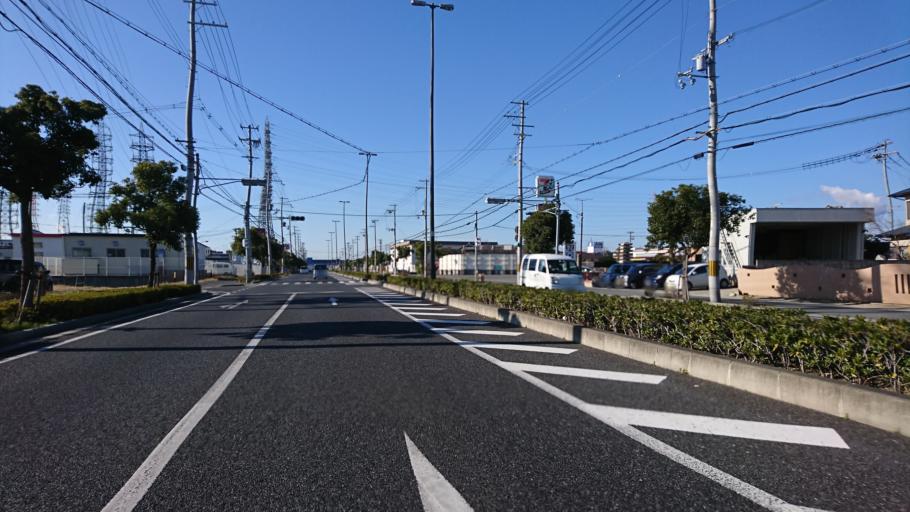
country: JP
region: Hyogo
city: Kakogawacho-honmachi
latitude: 34.7710
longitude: 134.8089
